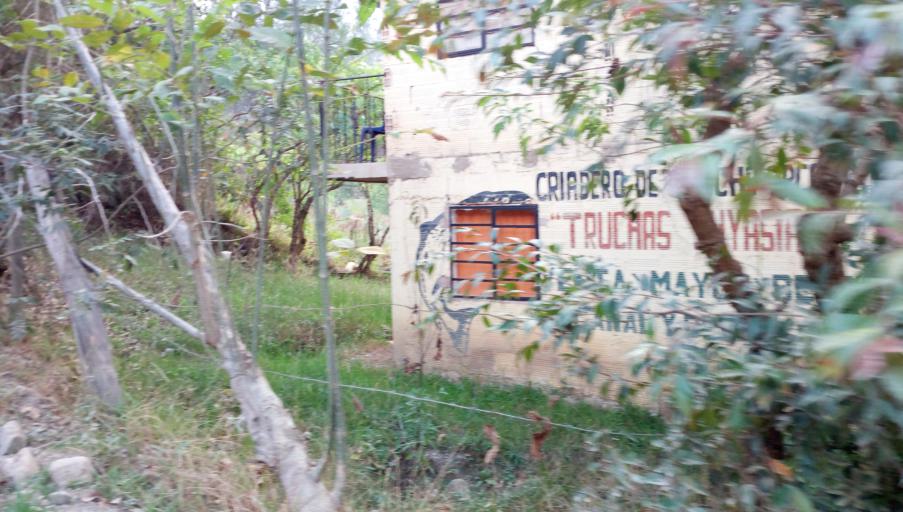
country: CO
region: Boyaca
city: Ramiriqui
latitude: 5.4133
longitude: -73.3263
